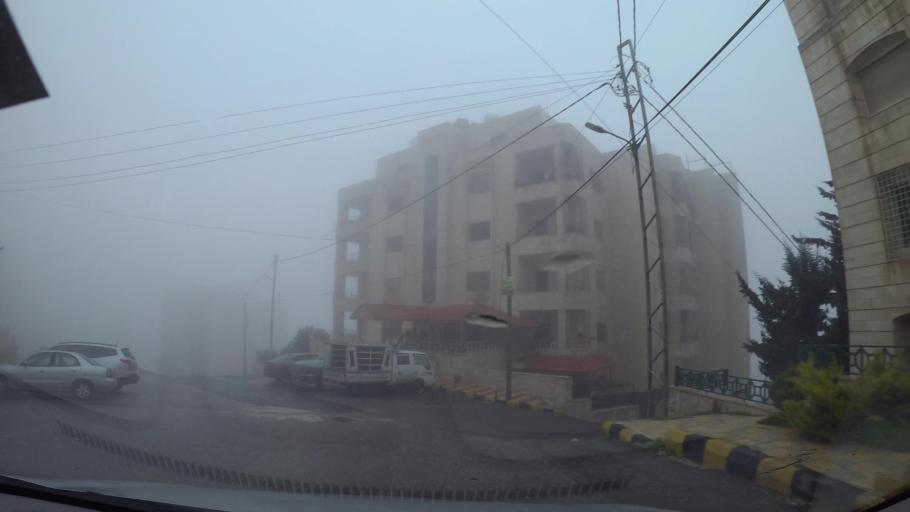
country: JO
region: Amman
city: Al Jubayhah
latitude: 32.0044
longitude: 35.8895
